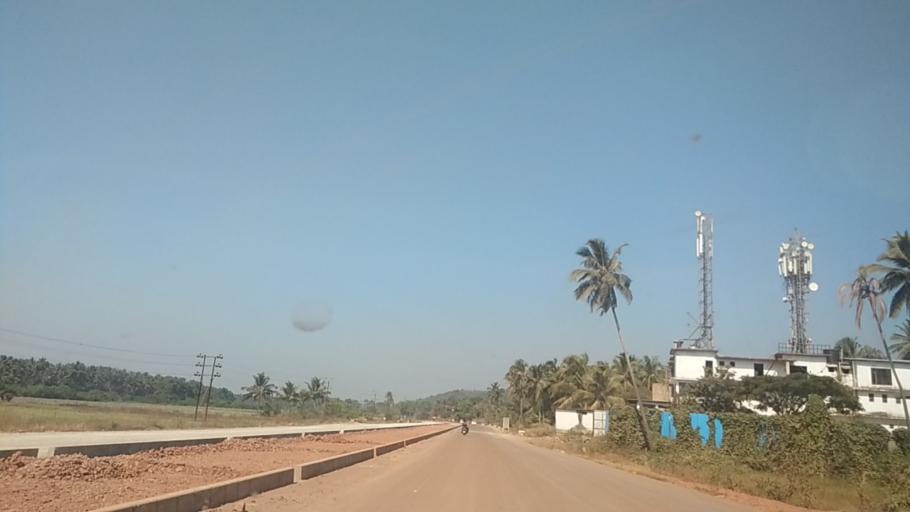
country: IN
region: Goa
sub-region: South Goa
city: Raia
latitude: 15.3183
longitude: 73.9407
